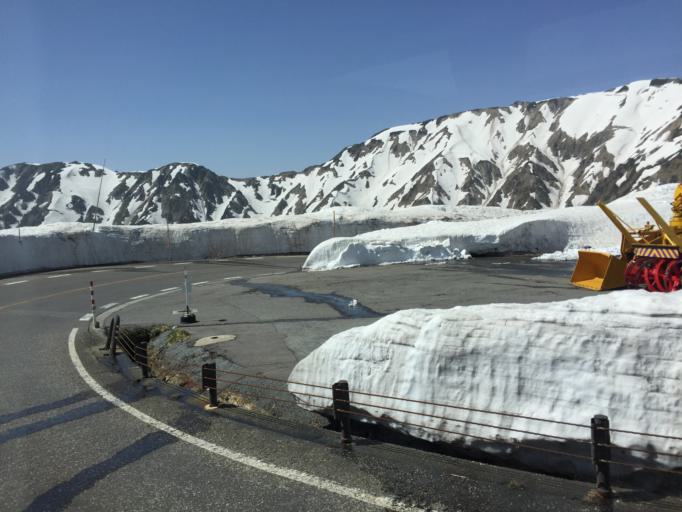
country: JP
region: Toyama
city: Kamiichi
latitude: 36.5804
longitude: 137.5794
